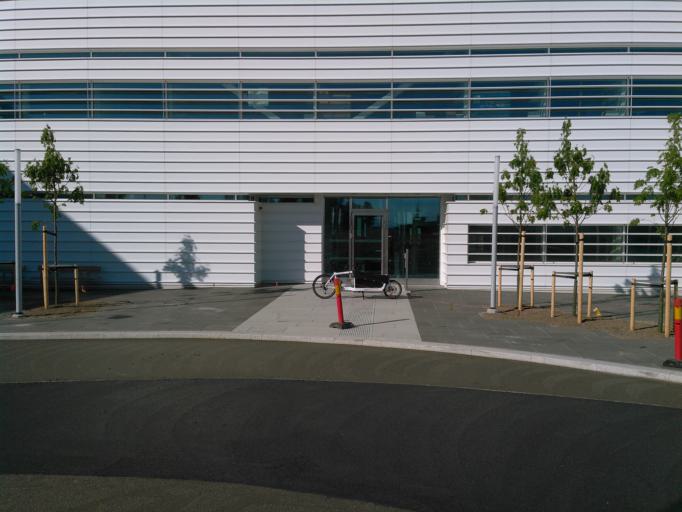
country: SE
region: Skane
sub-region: Lunds Kommun
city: Lund
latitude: 55.7269
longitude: 13.2353
